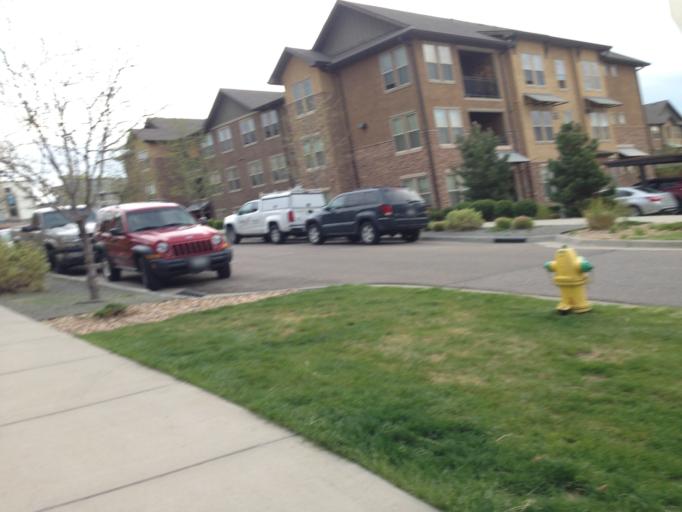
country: US
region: Colorado
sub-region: Jefferson County
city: Arvada
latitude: 39.7910
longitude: -105.1122
